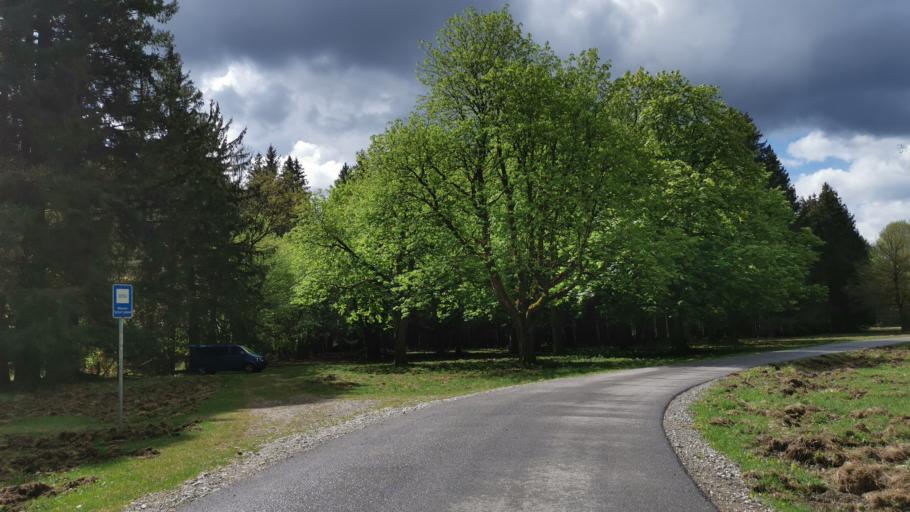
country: DE
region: Bavaria
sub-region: Upper Bavaria
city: Pullach im Isartal
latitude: 48.0597
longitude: 11.4897
